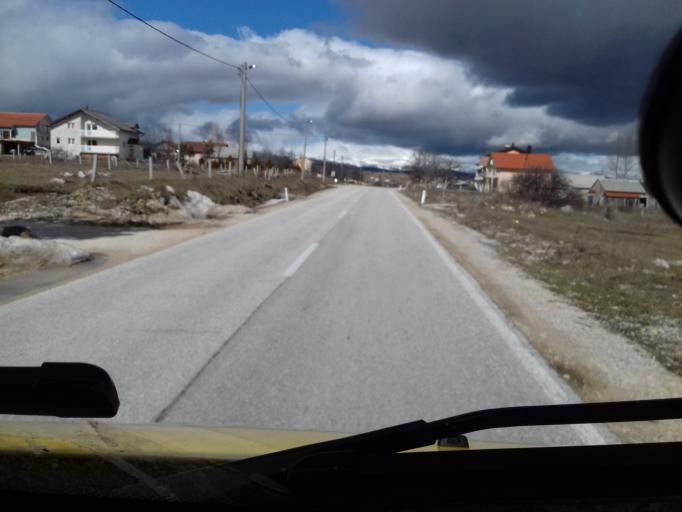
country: BA
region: Federation of Bosnia and Herzegovina
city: Dreznica
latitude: 43.6090
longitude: 17.2697
